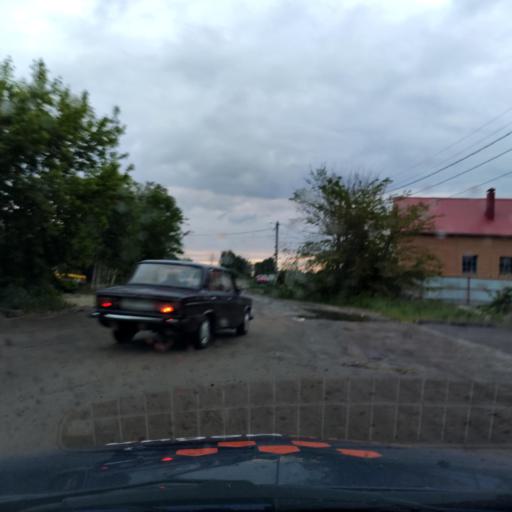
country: RU
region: Voronezj
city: Maslovka
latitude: 51.5472
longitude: 39.2397
